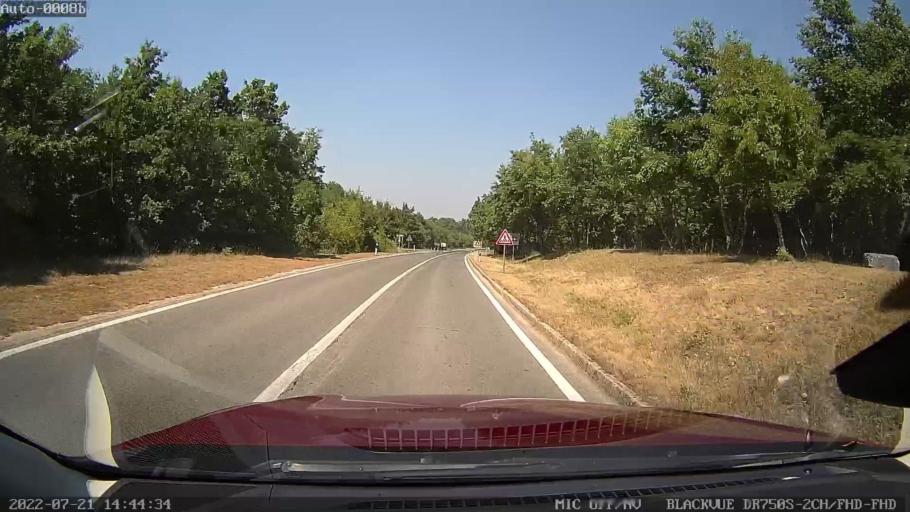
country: HR
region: Istarska
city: Pazin
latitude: 45.1189
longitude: 13.8844
